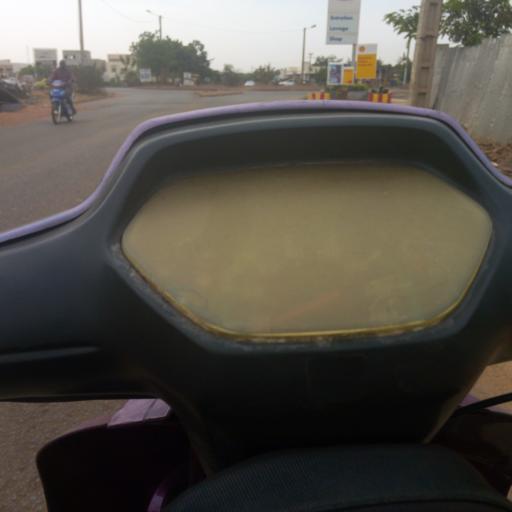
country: ML
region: Bamako
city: Bamako
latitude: 12.6541
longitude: -7.9363
